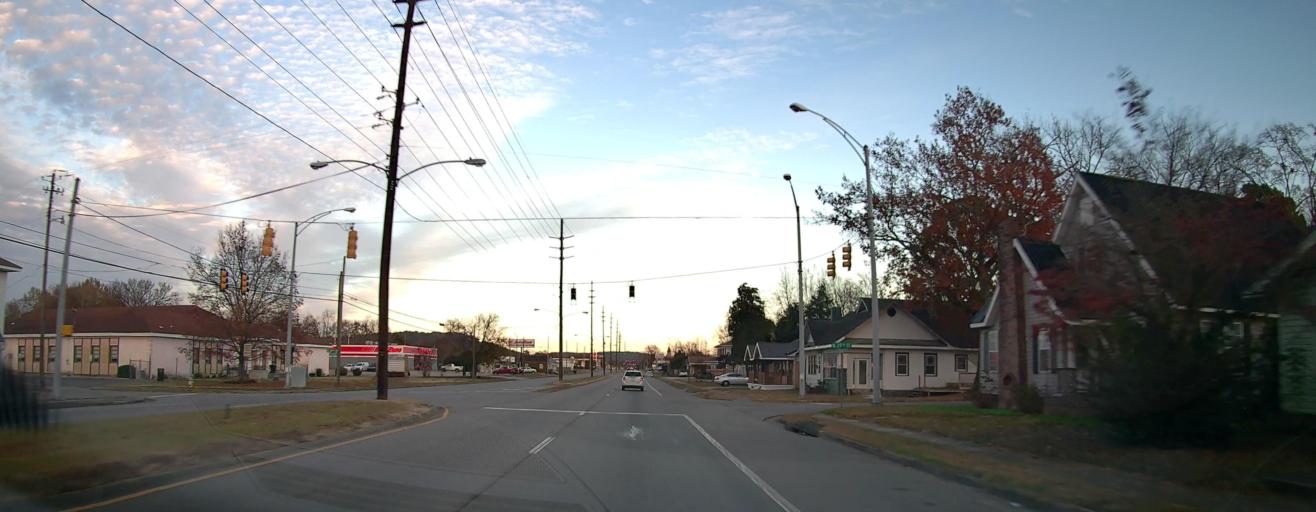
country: US
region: Alabama
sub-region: Etowah County
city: Attalla
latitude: 34.0224
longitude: -86.0508
